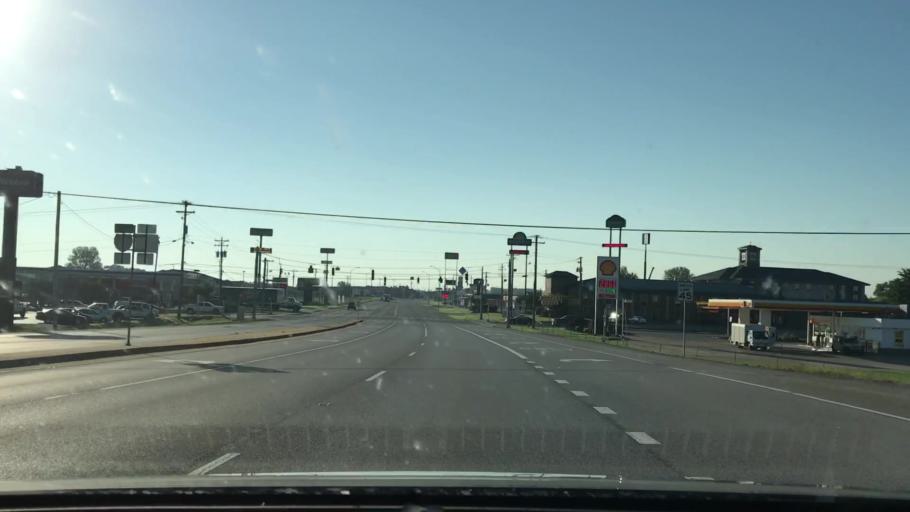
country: US
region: Kentucky
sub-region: Warren County
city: Plano
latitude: 36.9333
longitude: -86.4170
